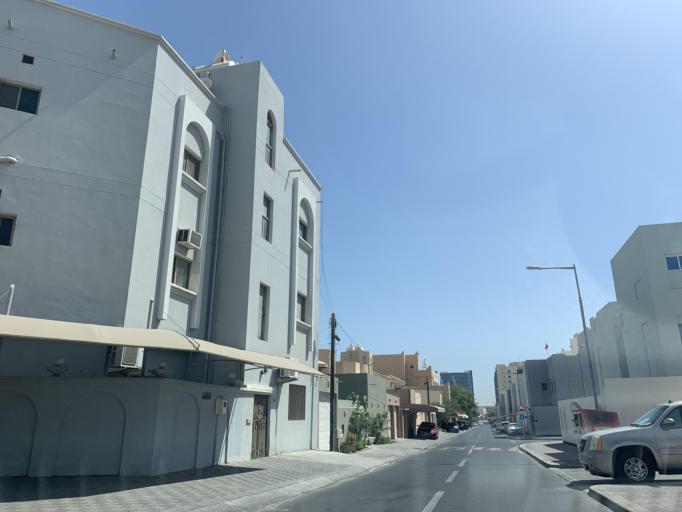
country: BH
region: Northern
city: Ar Rifa'
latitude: 26.1320
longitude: 50.5797
